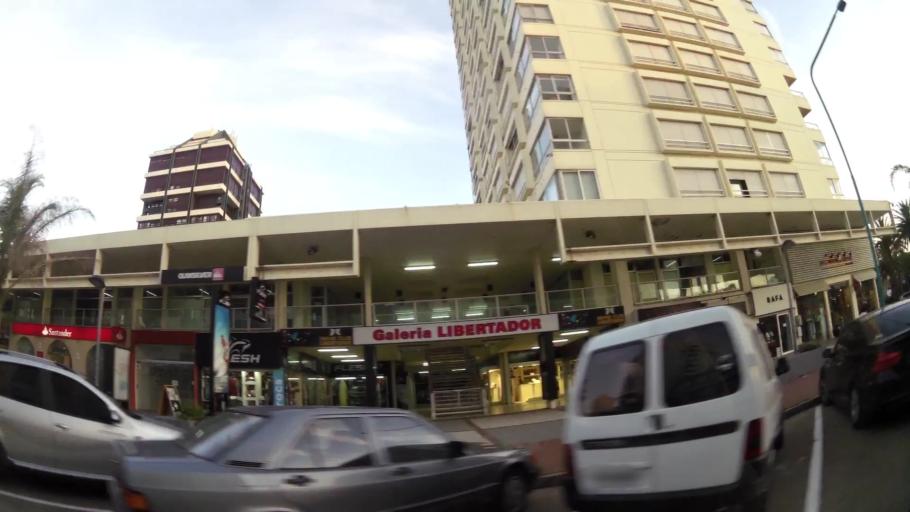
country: UY
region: Maldonado
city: Punta del Este
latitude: -34.9621
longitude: -54.9436
